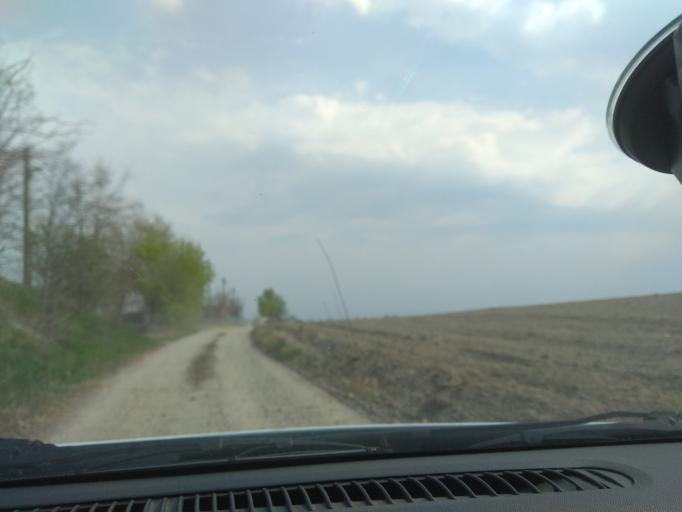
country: HU
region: Pest
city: Szigetszentmiklos
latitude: 47.3743
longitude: 19.0552
